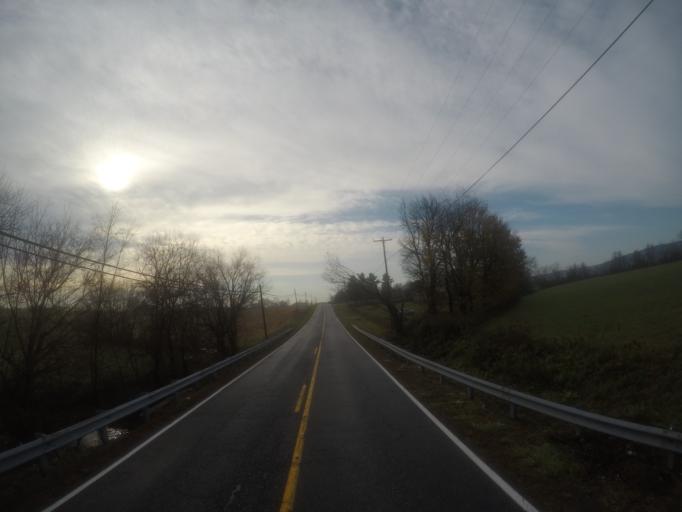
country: US
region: Maryland
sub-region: Frederick County
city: Walkersville
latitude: 39.5257
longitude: -77.4115
